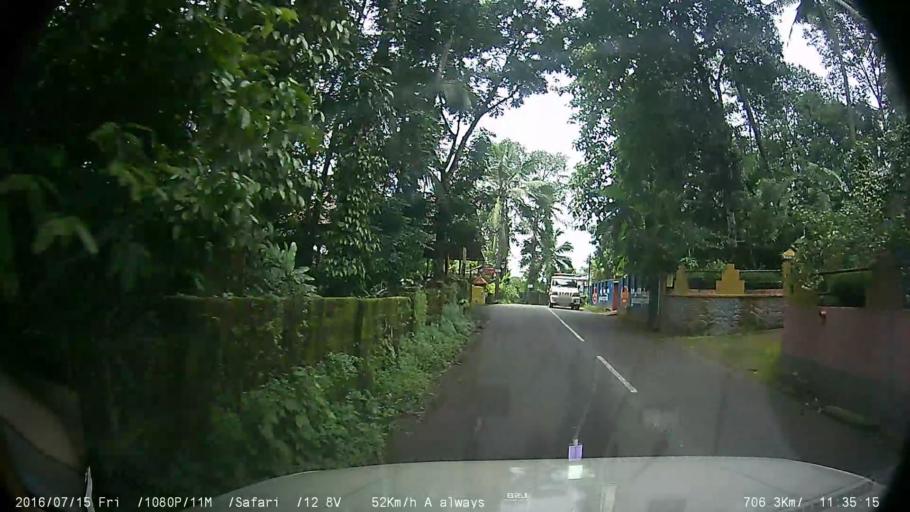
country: IN
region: Kerala
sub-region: Ernakulam
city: Piravam
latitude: 9.7781
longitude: 76.4977
